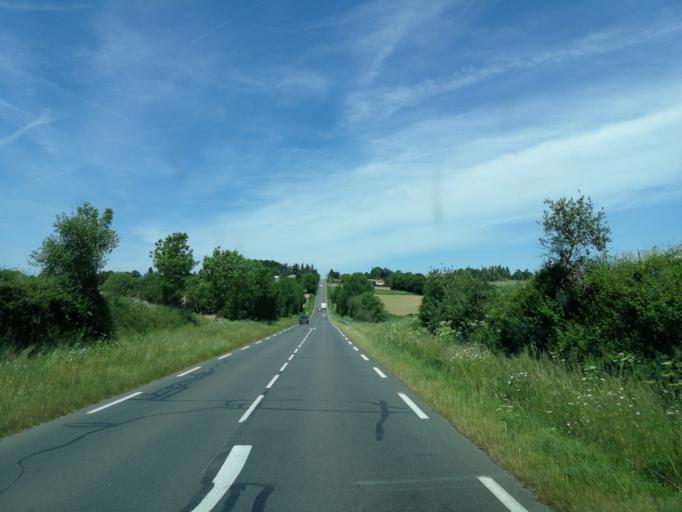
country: FR
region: Pays de la Loire
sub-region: Departement de la Vendee
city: Saint-Pierre-du-Chemin
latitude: 46.6837
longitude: -0.7119
